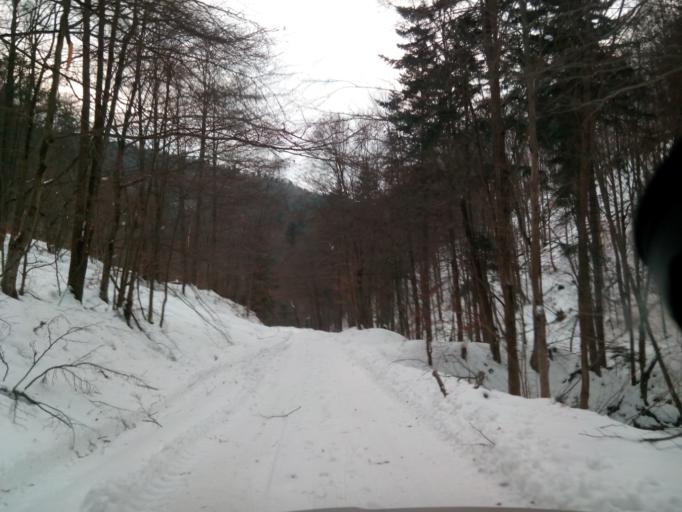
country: SK
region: Presovsky
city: Sabinov
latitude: 49.2101
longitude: 21.1015
